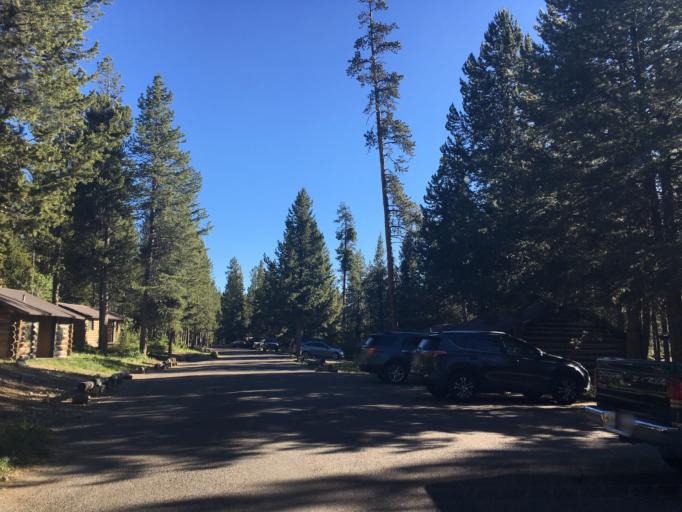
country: US
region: Wyoming
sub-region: Teton County
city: Moose Wilson Road
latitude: 43.9038
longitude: -110.6400
